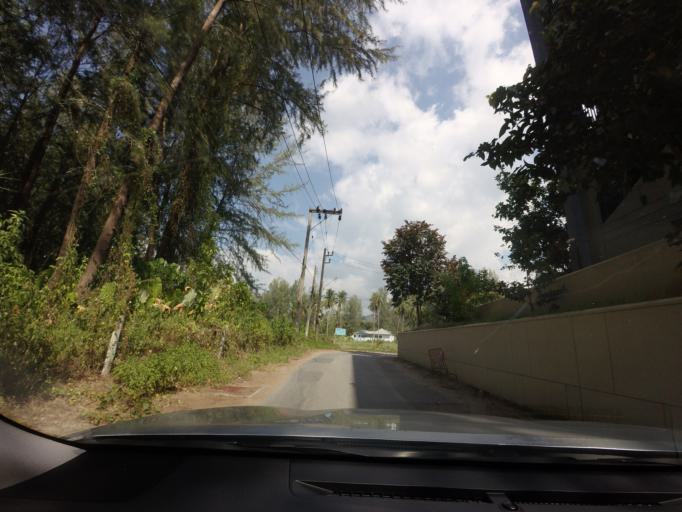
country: TH
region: Phangnga
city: Ban Khao Lak
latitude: 8.6617
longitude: 98.2479
